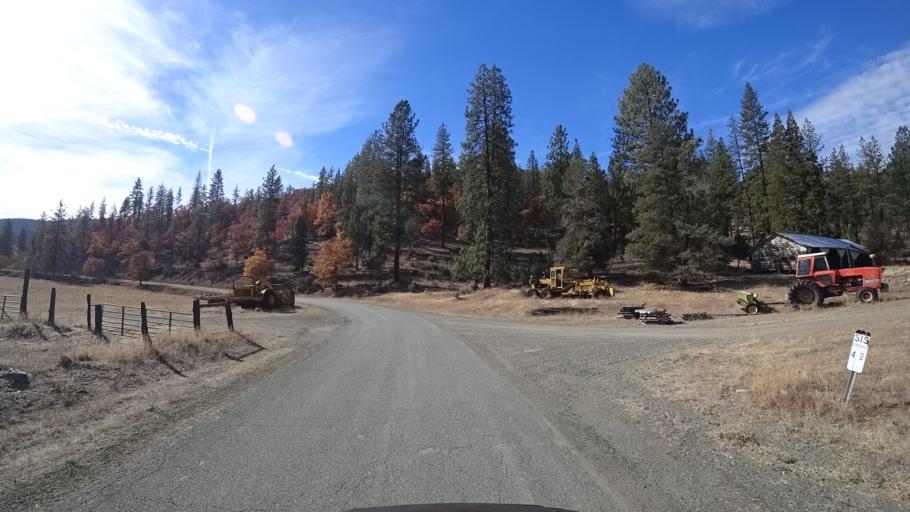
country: US
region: California
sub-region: Siskiyou County
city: Yreka
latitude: 41.6080
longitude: -122.7370
